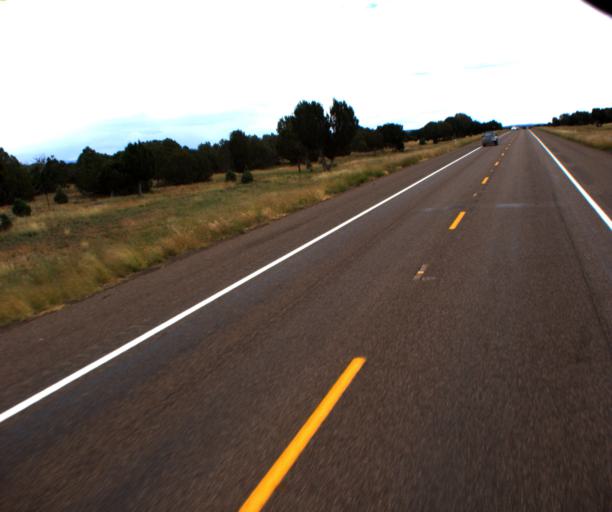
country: US
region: Arizona
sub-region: Navajo County
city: Show Low
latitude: 34.2982
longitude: -110.0342
